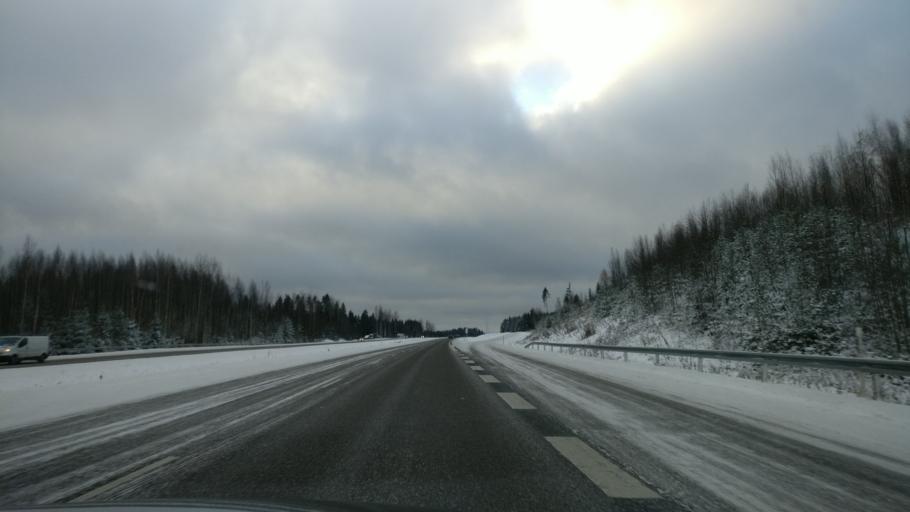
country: FI
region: Paijanne Tavastia
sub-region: Lahti
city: Nastola
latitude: 61.0703
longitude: 25.8803
